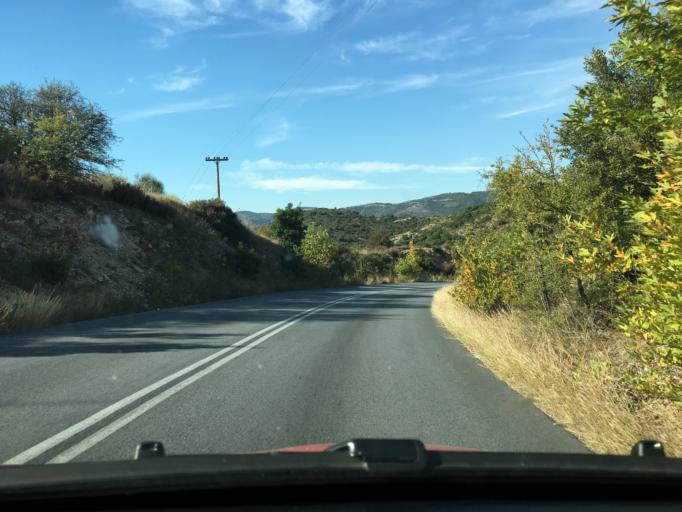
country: GR
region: Central Macedonia
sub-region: Nomos Chalkidikis
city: Megali Panagia
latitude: 40.3826
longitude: 23.7206
